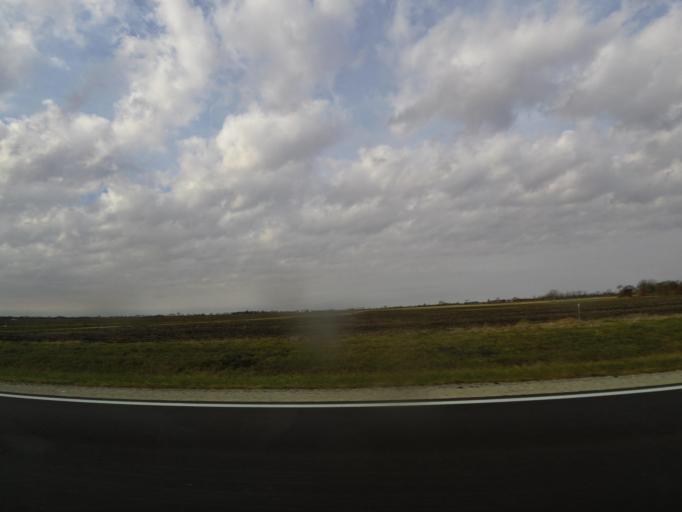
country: US
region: Illinois
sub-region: Christian County
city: Pana
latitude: 39.3471
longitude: -89.0817
